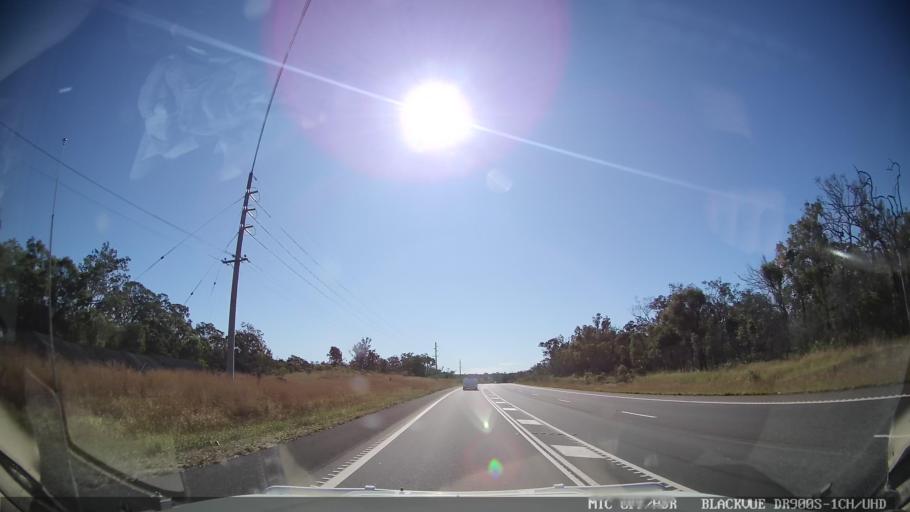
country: AU
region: Queensland
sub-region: Bundaberg
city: Childers
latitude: -25.2720
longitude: 152.3790
